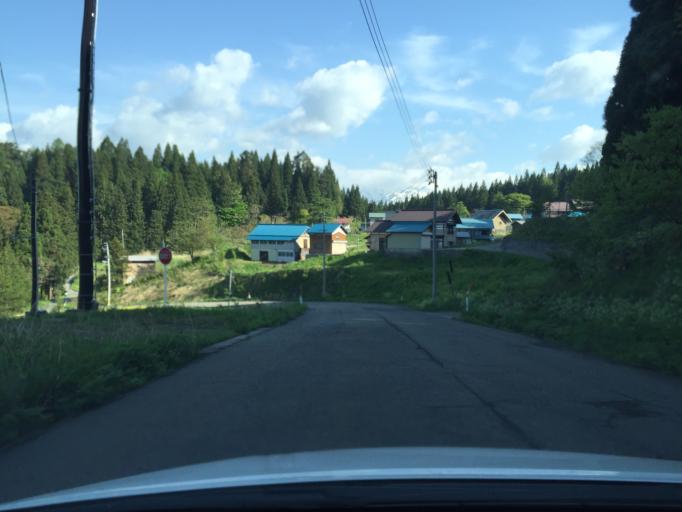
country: JP
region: Fukushima
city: Kitakata
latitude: 37.6831
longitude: 139.6847
